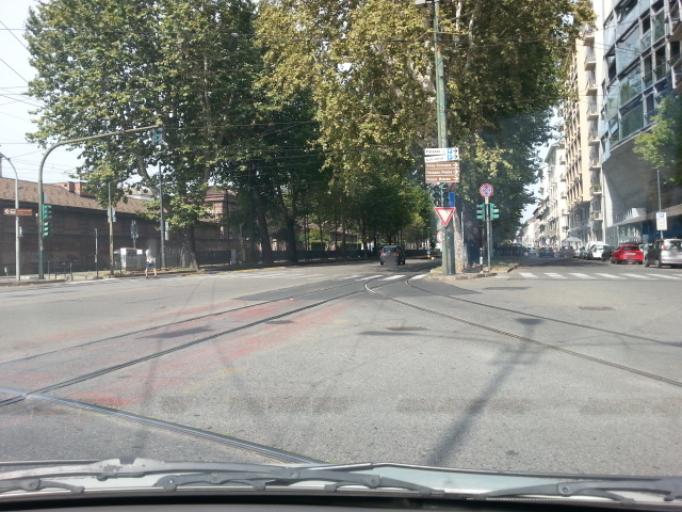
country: IT
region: Piedmont
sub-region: Provincia di Torino
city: Turin
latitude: 45.0750
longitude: 7.6894
